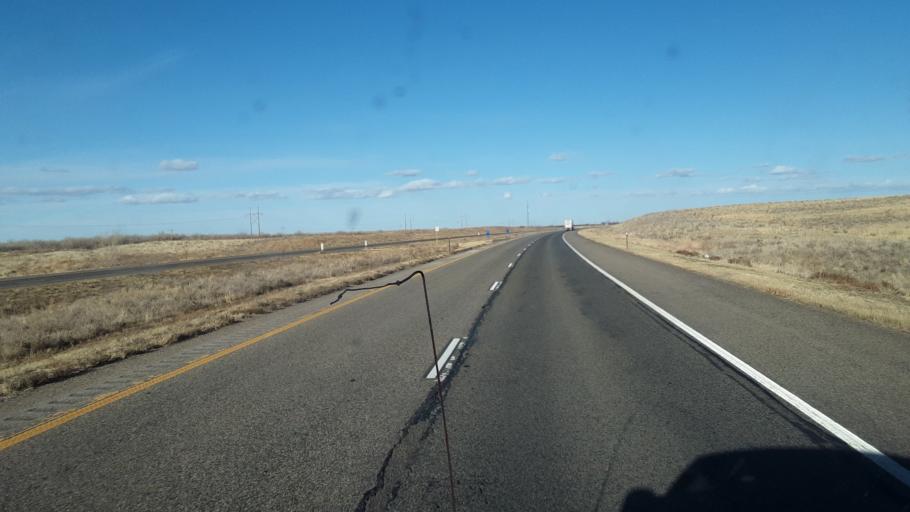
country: US
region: Colorado
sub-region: Logan County
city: Sterling
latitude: 40.6511
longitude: -103.1463
